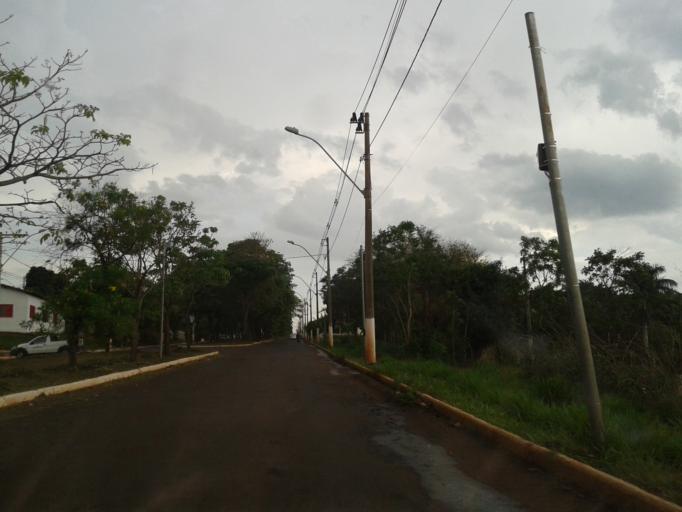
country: BR
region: Minas Gerais
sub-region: Ituiutaba
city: Ituiutaba
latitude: -18.9675
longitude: -49.4735
